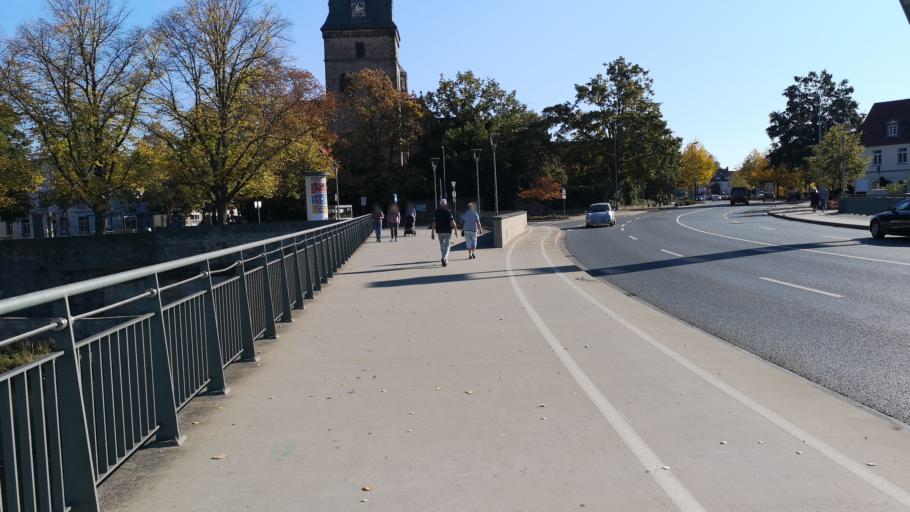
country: DE
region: Lower Saxony
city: Hameln
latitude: 52.1016
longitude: 9.3526
